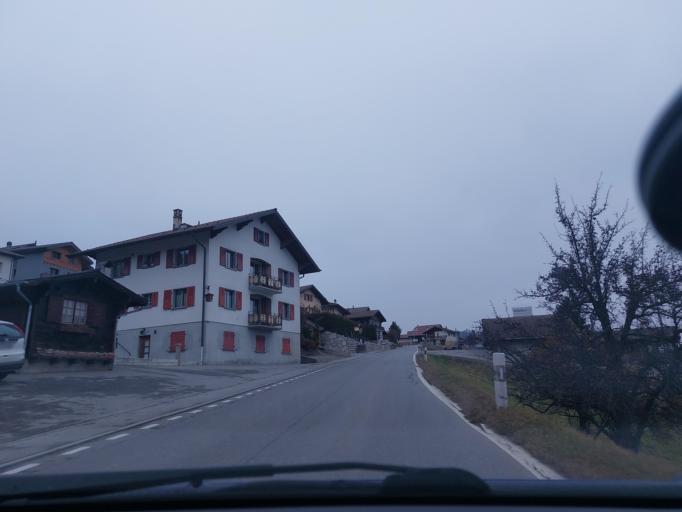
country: CH
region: Valais
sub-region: Conthey District
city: Basse-Nendaz
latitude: 46.1872
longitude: 7.3026
